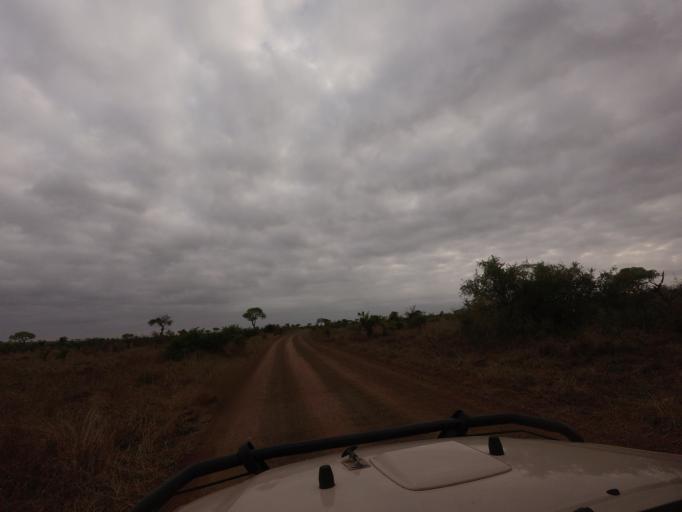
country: ZA
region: Mpumalanga
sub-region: Ehlanzeni District
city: Komatipoort
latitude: -25.3004
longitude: 31.9191
